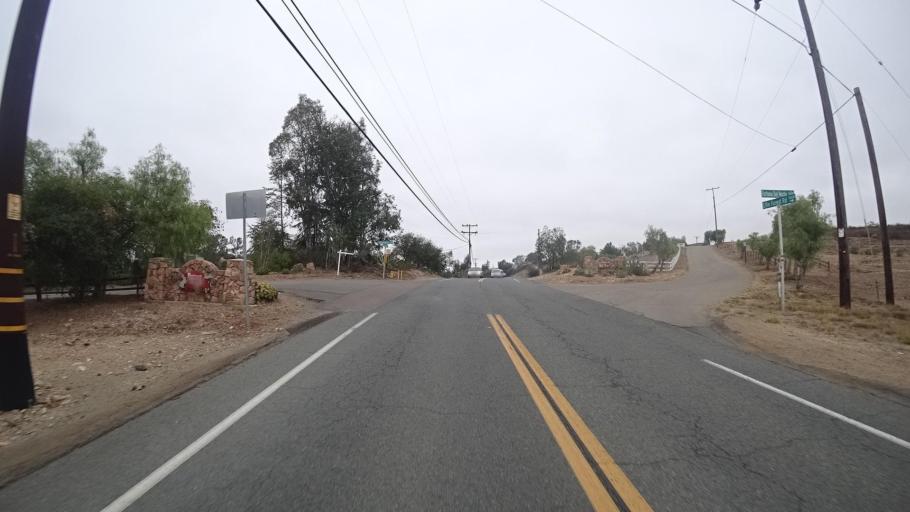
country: US
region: California
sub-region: San Diego County
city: Lake San Marcos
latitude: 33.0857
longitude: -117.1866
